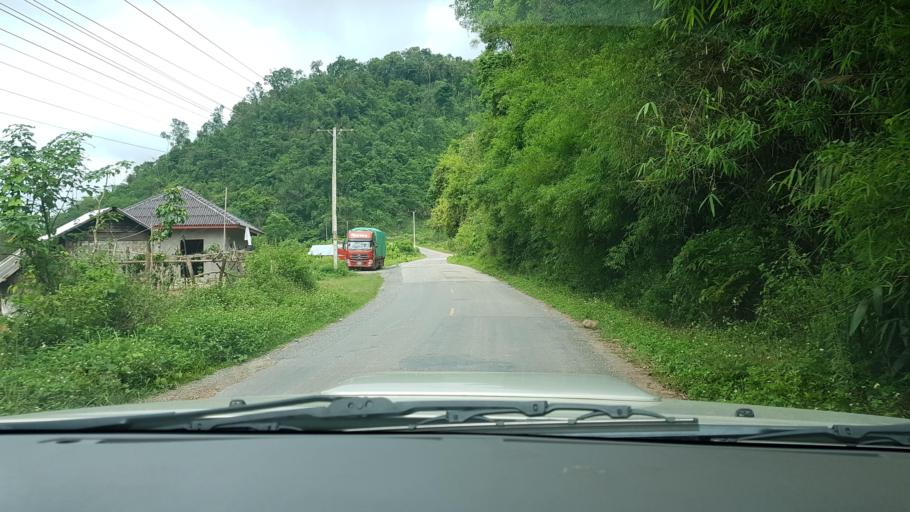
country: LA
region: Oudomxai
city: Muang Xay
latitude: 20.5584
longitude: 101.9138
